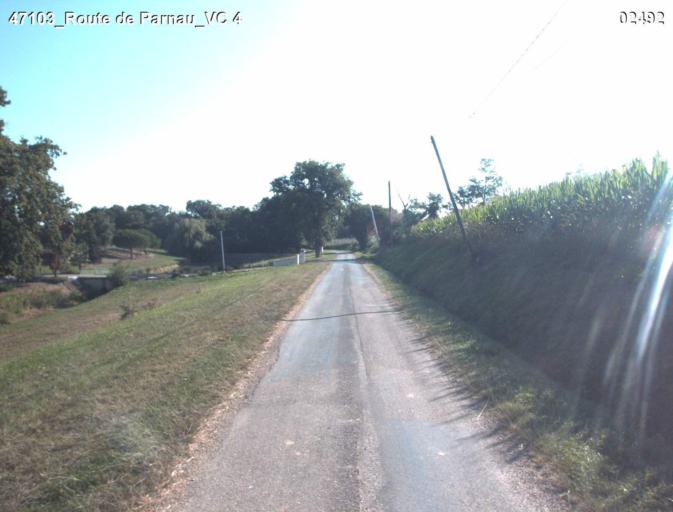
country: FR
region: Aquitaine
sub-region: Departement du Lot-et-Garonne
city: Nerac
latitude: 44.0802
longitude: 0.3580
